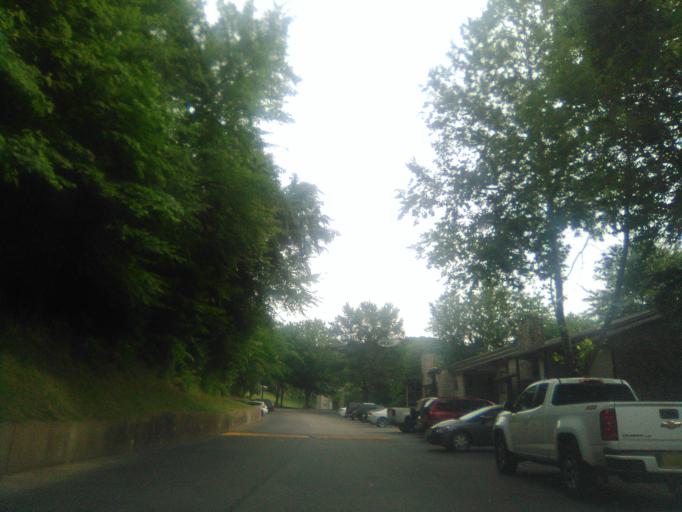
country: US
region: Tennessee
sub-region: Davidson County
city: Belle Meade
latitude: 36.0822
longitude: -86.9089
